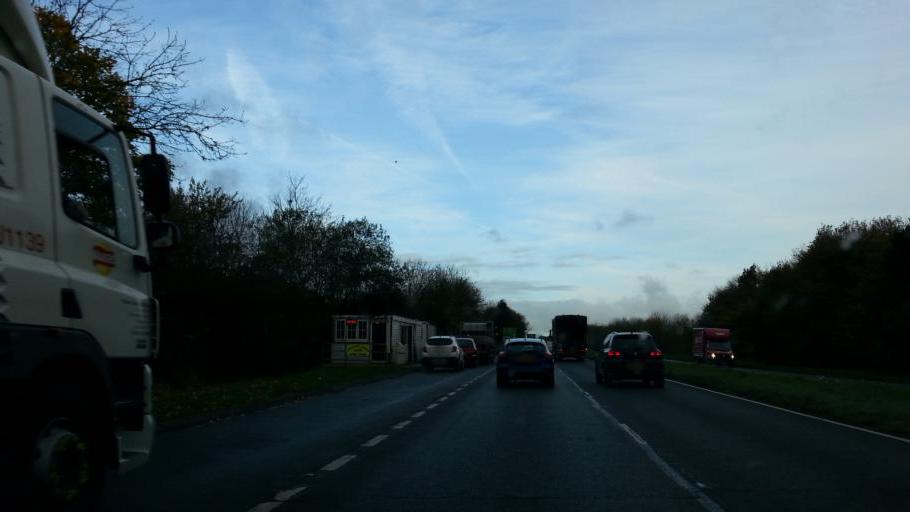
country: GB
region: England
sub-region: Leicestershire
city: Markfield
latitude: 52.6901
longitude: -1.2733
